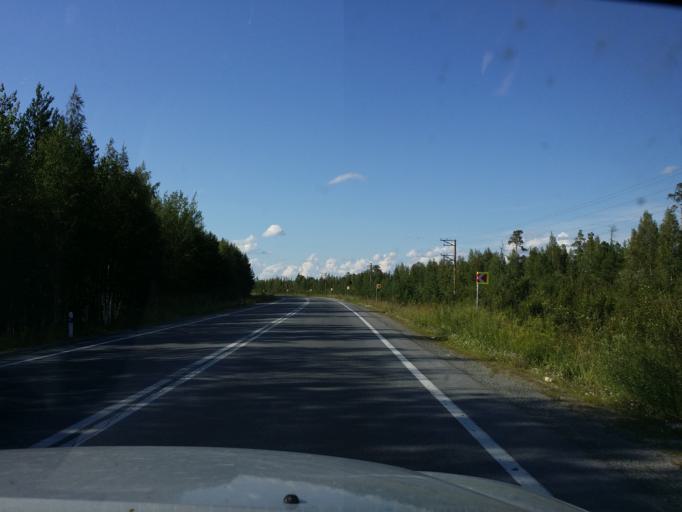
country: RU
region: Khanty-Mansiyskiy Avtonomnyy Okrug
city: Lokosovo
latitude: 61.3860
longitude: 74.9201
